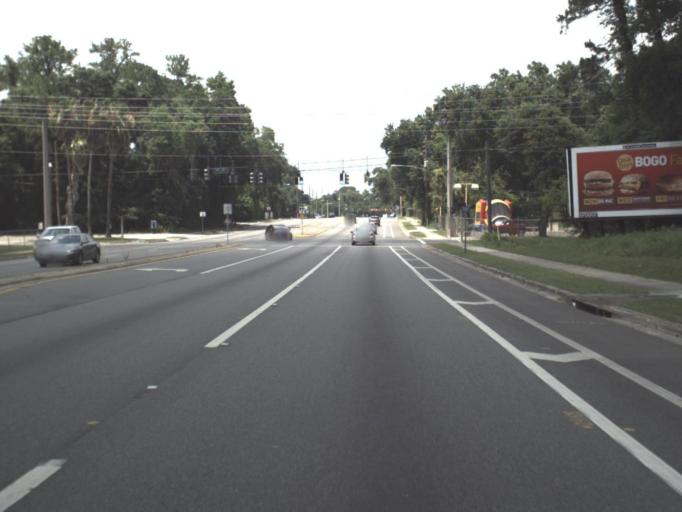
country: US
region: Florida
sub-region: Alachua County
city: Gainesville
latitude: 29.6474
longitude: -82.3114
